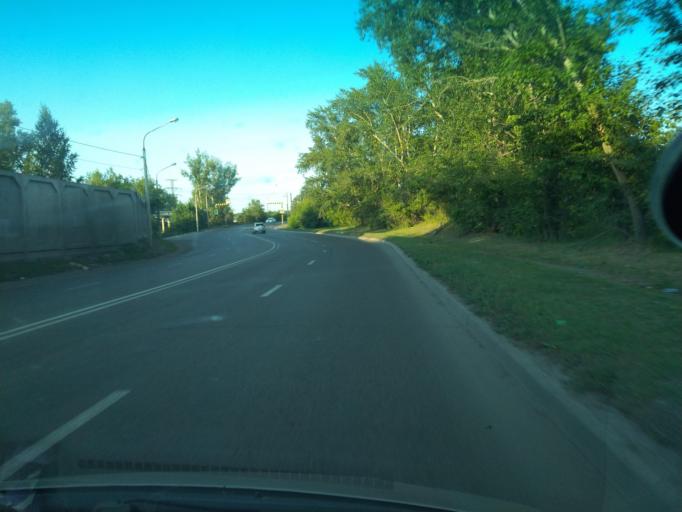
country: RU
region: Krasnoyarskiy
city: Berezovka
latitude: 56.0151
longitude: 93.0258
